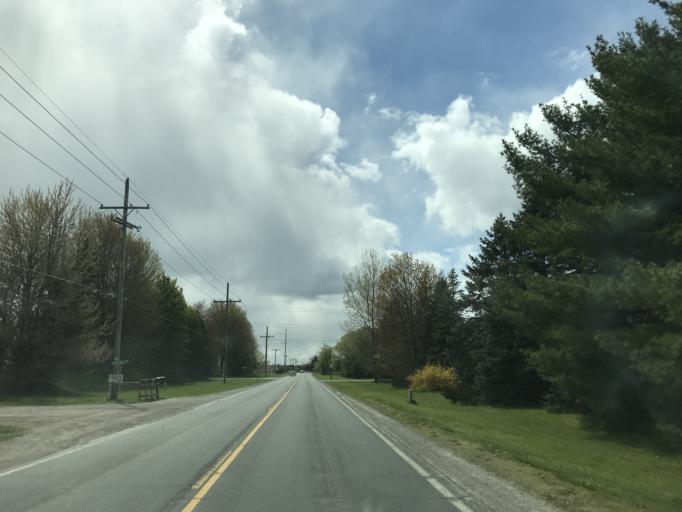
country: US
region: Michigan
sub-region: Wayne County
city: Plymouth
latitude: 42.3743
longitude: -83.5601
